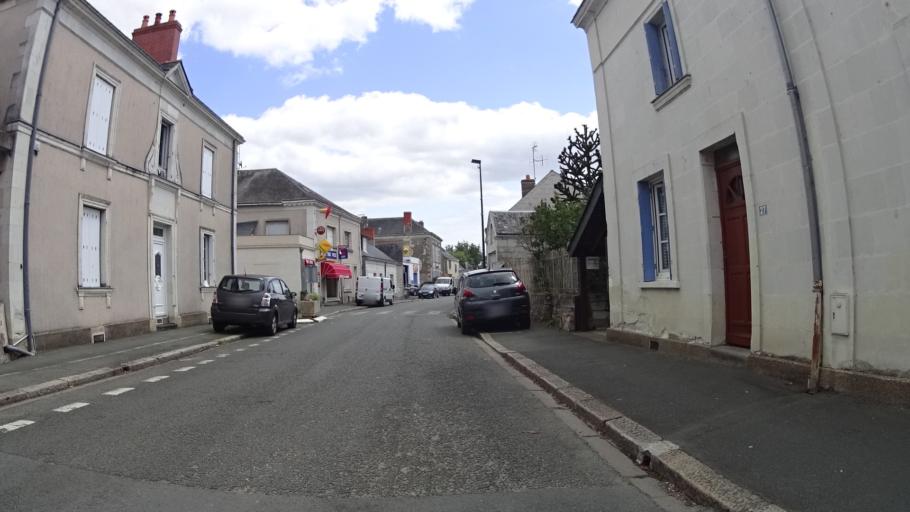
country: FR
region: Pays de la Loire
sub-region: Departement de Maine-et-Loire
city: La Dagueniere
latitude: 47.4194
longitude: -0.4347
